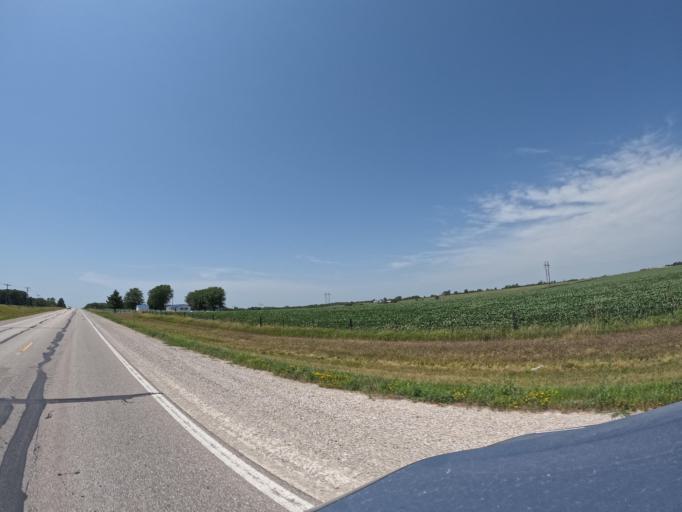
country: US
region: Iowa
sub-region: Henry County
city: Mount Pleasant
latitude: 40.9671
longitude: -91.6156
